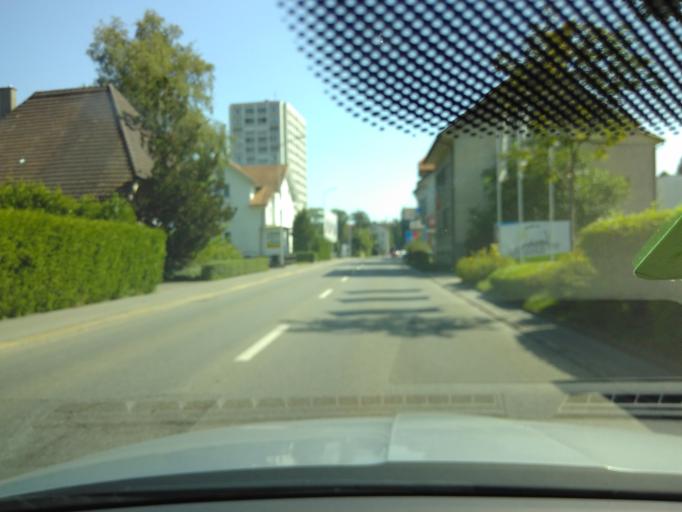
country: CH
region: Aargau
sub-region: Bezirk Kulm
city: Reinach
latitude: 47.2599
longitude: 8.1787
